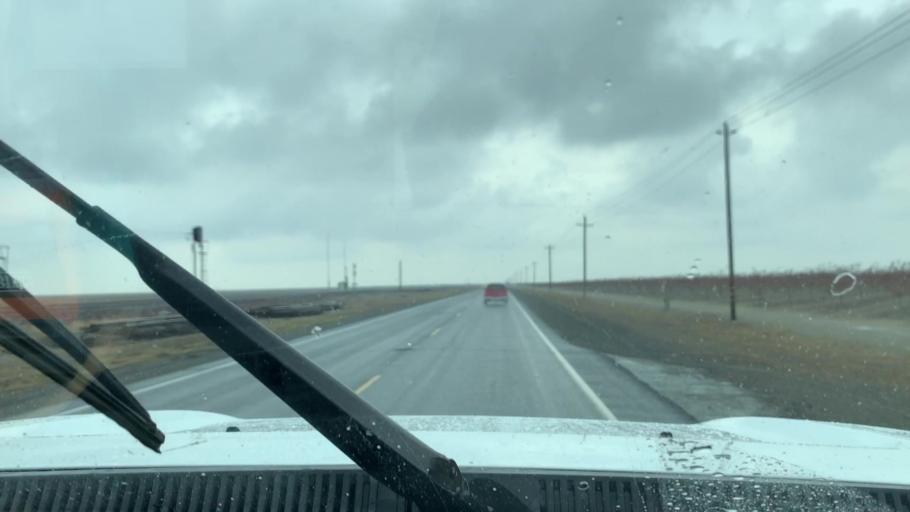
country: US
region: California
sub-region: Tulare County
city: Alpaugh
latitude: 35.9976
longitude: -119.4828
